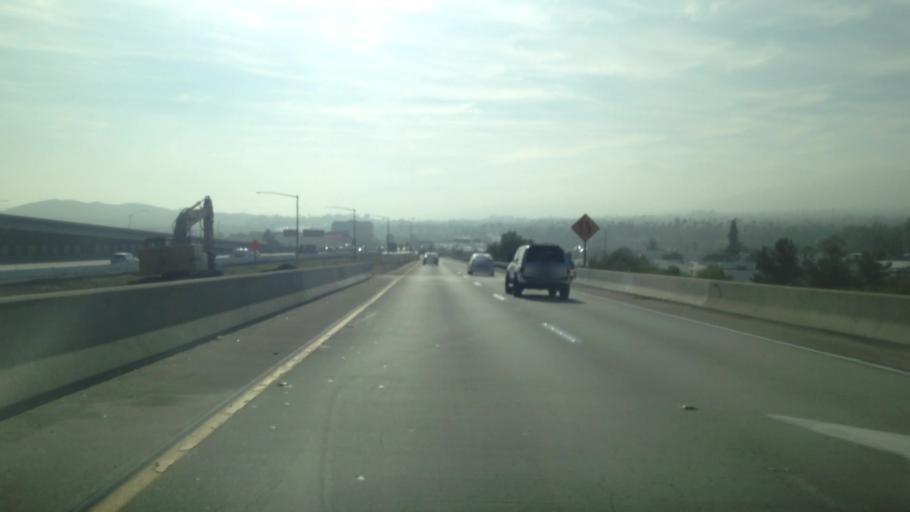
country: US
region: California
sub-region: Riverside County
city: Corona
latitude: 33.8785
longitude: -117.5470
